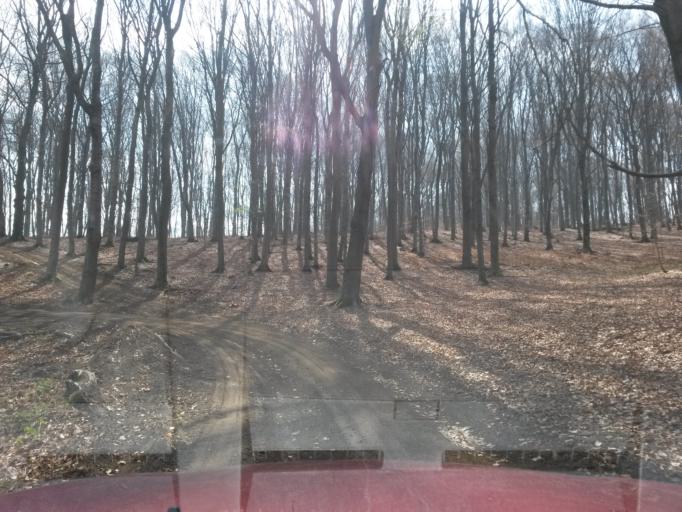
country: SK
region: Presovsky
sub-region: Okres Presov
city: Presov
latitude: 48.9308
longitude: 21.1405
